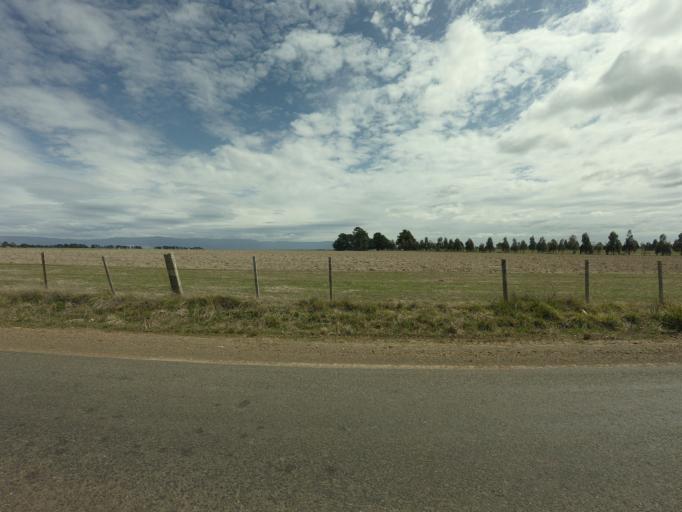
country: AU
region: Tasmania
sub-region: Northern Midlands
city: Longford
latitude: -41.7046
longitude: 147.1966
